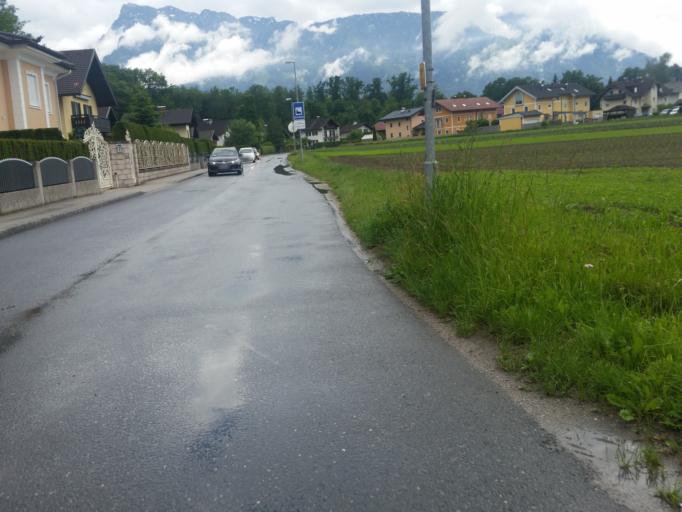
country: AT
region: Salzburg
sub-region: Salzburg Stadt
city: Salzburg
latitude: 47.7849
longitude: 12.9988
